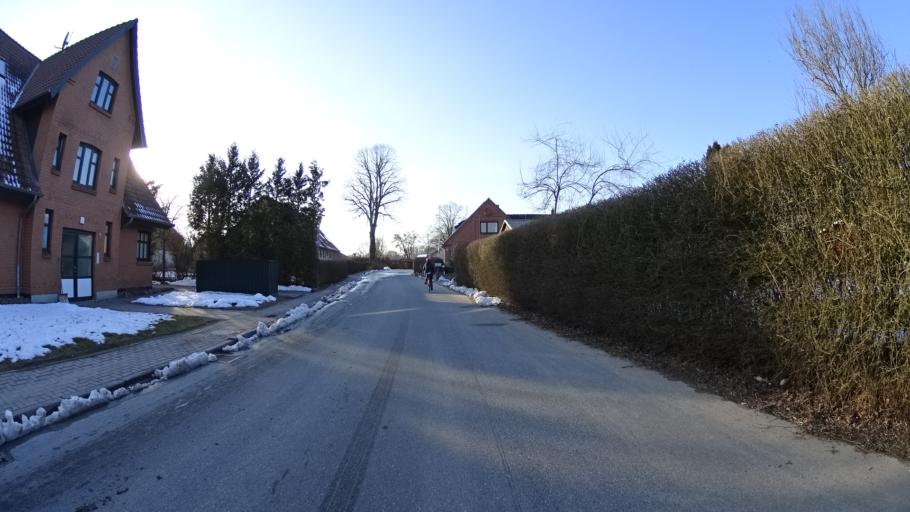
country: DE
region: Schleswig-Holstein
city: Fargau-Pratjau
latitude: 54.3285
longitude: 10.4163
